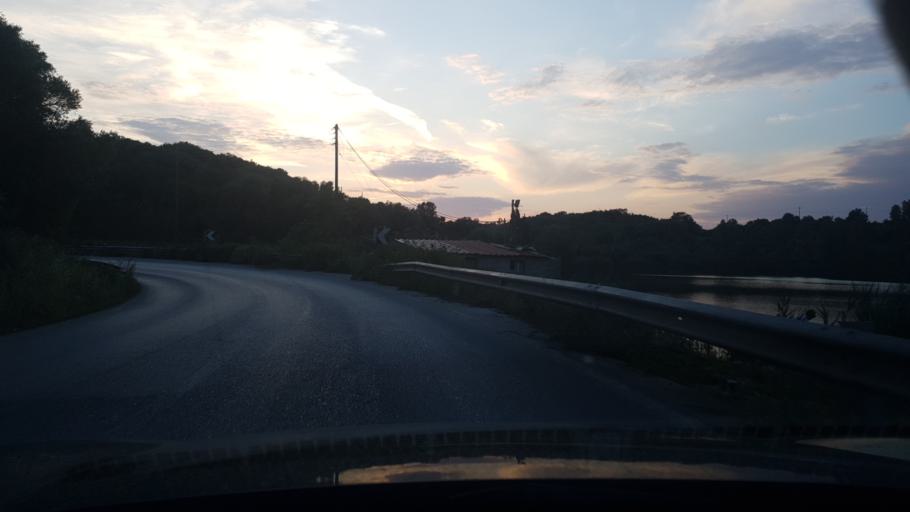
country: GR
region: West Greece
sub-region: Nomos Aitolias kai Akarnanias
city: Vonitsa
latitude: 38.9180
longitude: 20.8622
